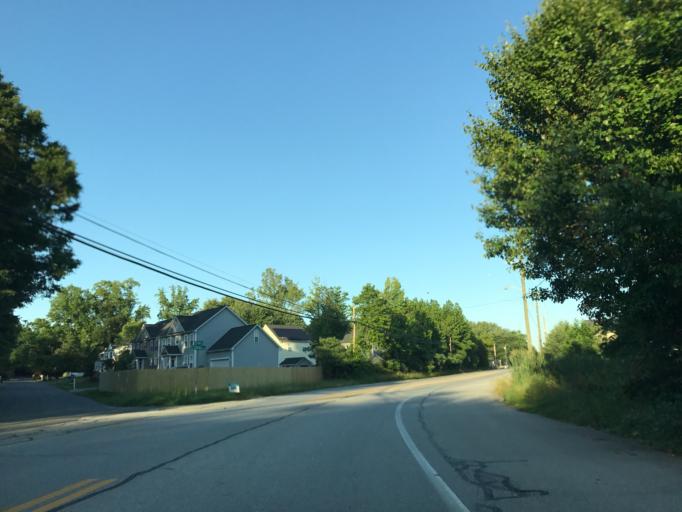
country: US
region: Maryland
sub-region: Anne Arundel County
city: Selby-on-the-Bay
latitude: 38.9061
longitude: -76.5267
